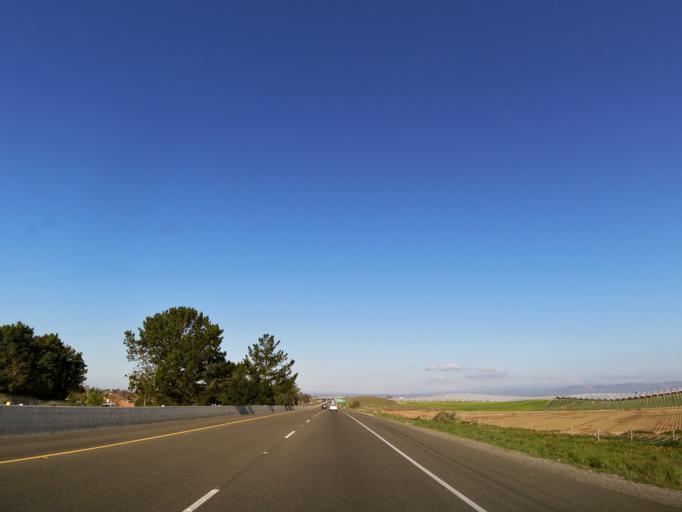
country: US
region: California
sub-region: Santa Barbara County
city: Orcutt
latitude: 34.8699
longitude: -120.3999
